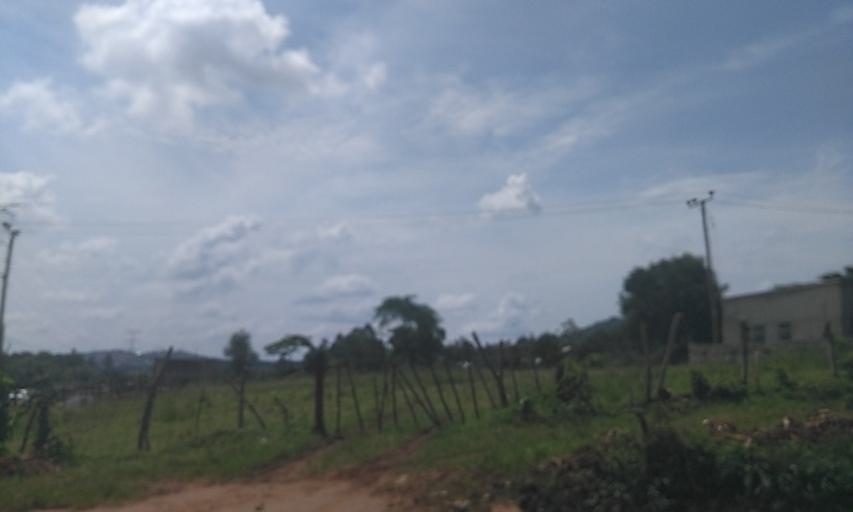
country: UG
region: Central Region
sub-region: Wakiso District
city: Wakiso
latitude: 0.3942
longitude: 32.5005
